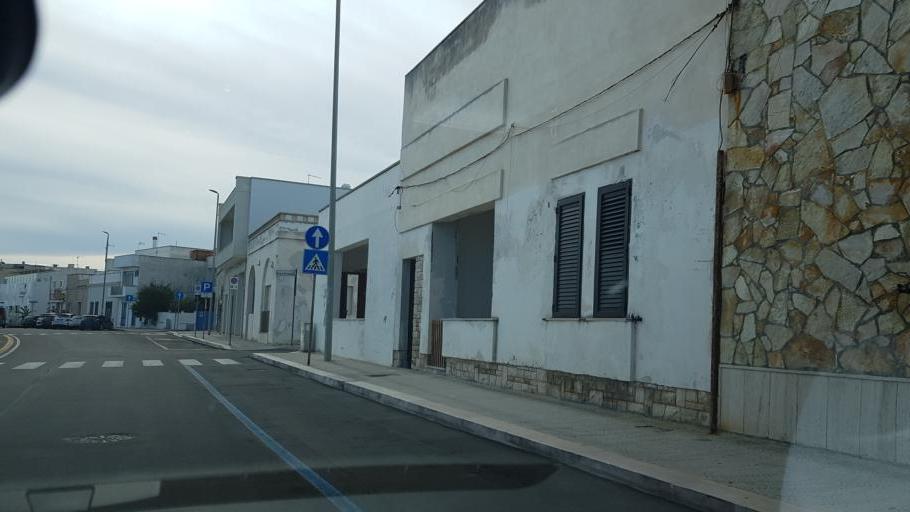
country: IT
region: Apulia
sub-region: Provincia di Lecce
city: Borgagne
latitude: 40.3039
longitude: 18.4005
